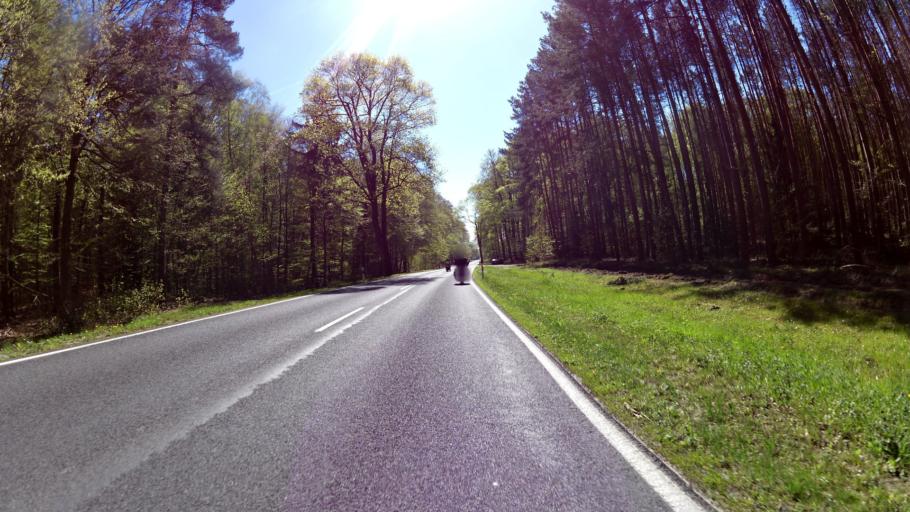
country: DE
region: Brandenburg
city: Wandlitz
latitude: 52.7210
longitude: 13.5196
